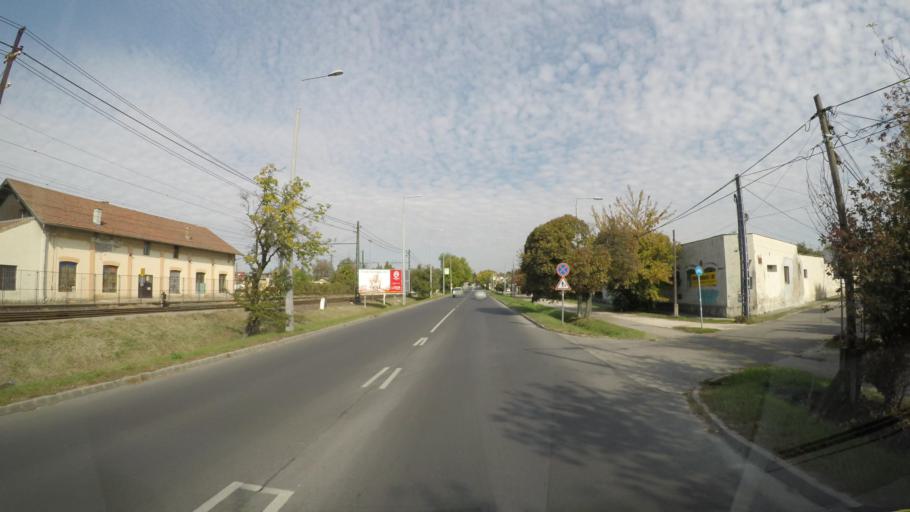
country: HU
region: Pest
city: Csomor
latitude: 47.5181
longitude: 19.2147
